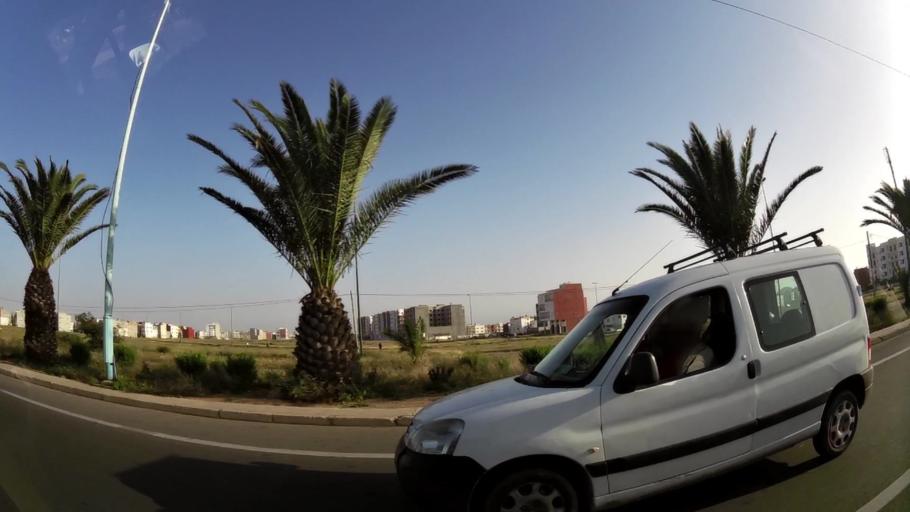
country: MA
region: Oued ed Dahab-Lagouira
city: Dakhla
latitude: 30.4033
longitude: -9.5717
